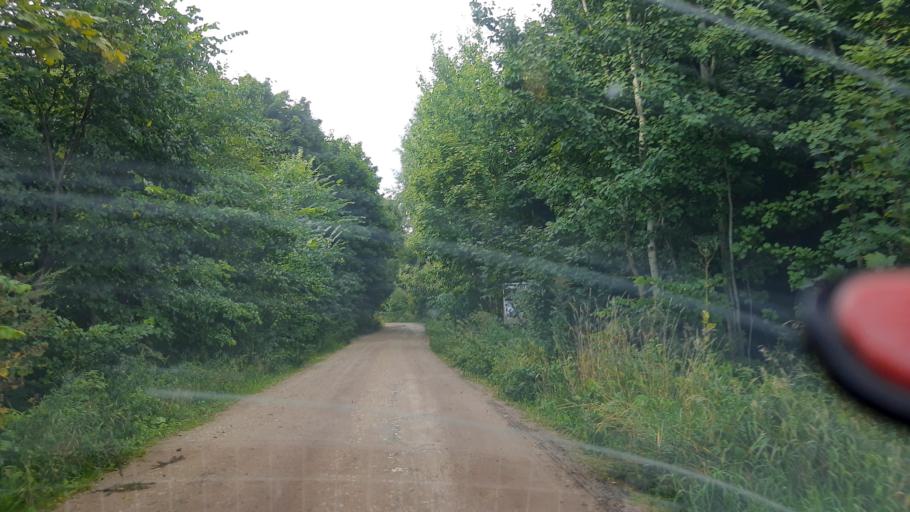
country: RU
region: Bashkortostan
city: Iglino
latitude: 54.7686
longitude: 56.4536
